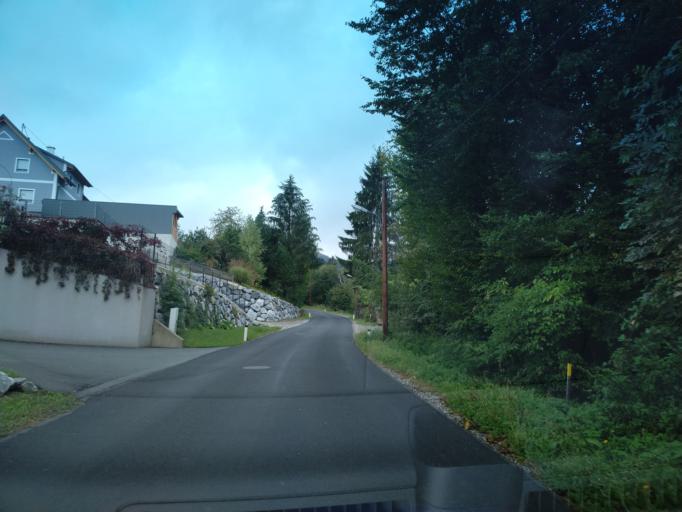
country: AT
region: Styria
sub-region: Politischer Bezirk Deutschlandsberg
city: Deutschlandsberg
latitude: 46.8226
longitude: 15.2054
